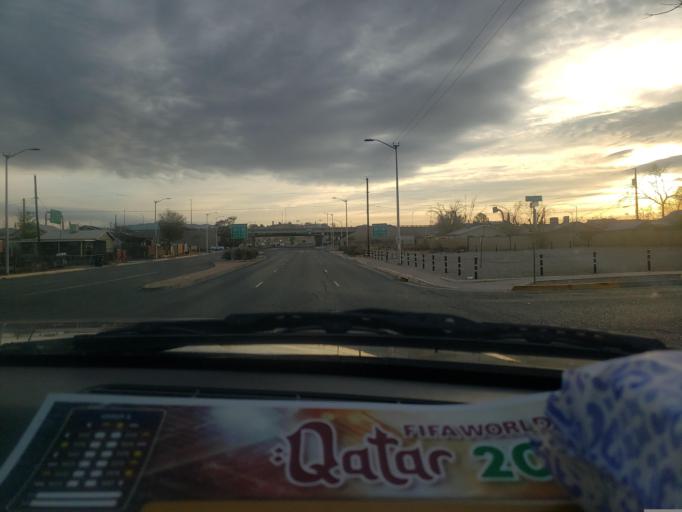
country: US
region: New Mexico
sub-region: Bernalillo County
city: Albuquerque
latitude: 35.0696
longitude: -106.6421
